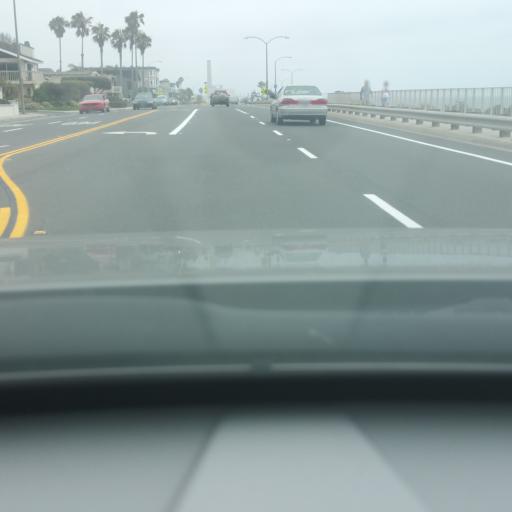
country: US
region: California
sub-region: San Diego County
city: Carlsbad
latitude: 33.1516
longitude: -117.3486
